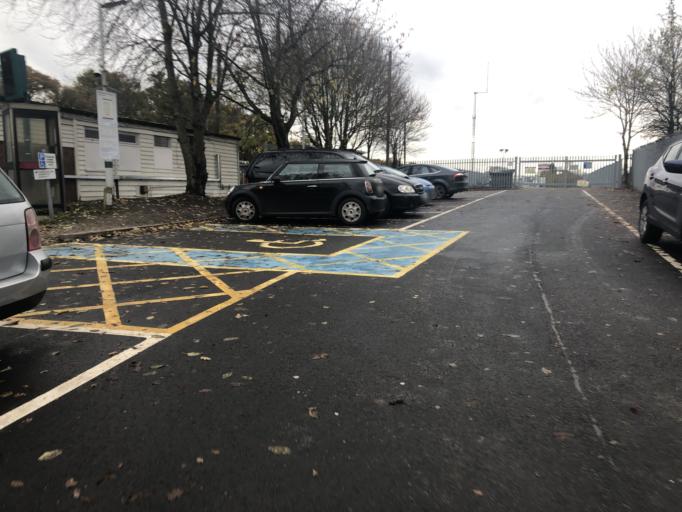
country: GB
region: England
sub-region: Surrey
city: Salfords
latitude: 51.2019
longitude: -0.1628
